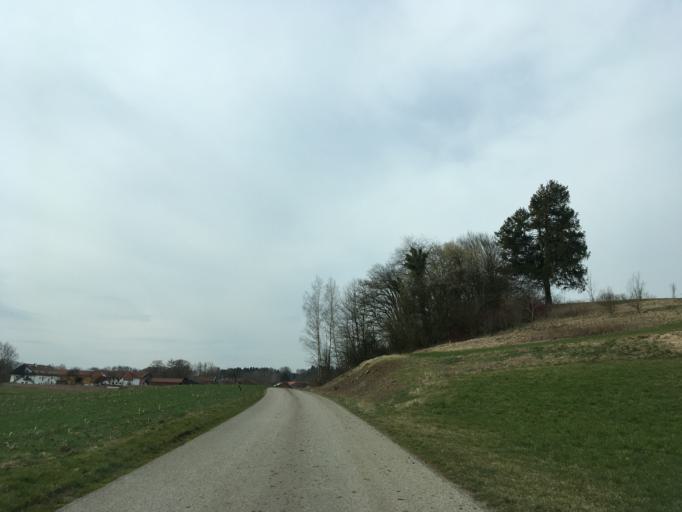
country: DE
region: Bavaria
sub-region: Upper Bavaria
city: Eggstatt
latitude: 47.9440
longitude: 12.3825
